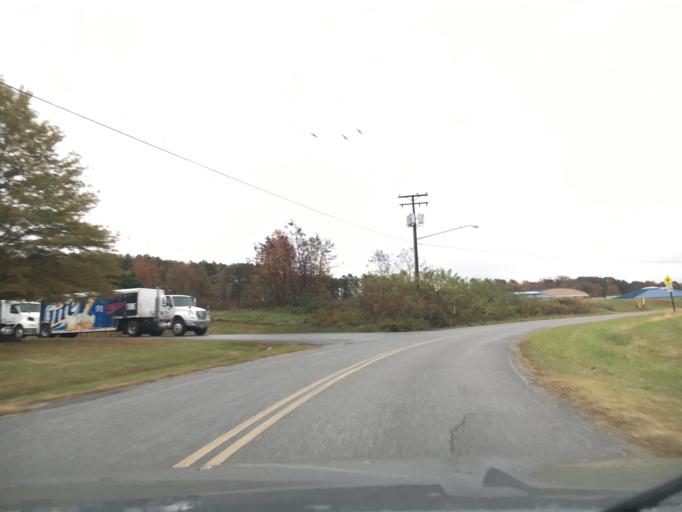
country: US
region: Virginia
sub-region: Halifax County
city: South Boston
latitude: 36.7209
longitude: -78.8920
